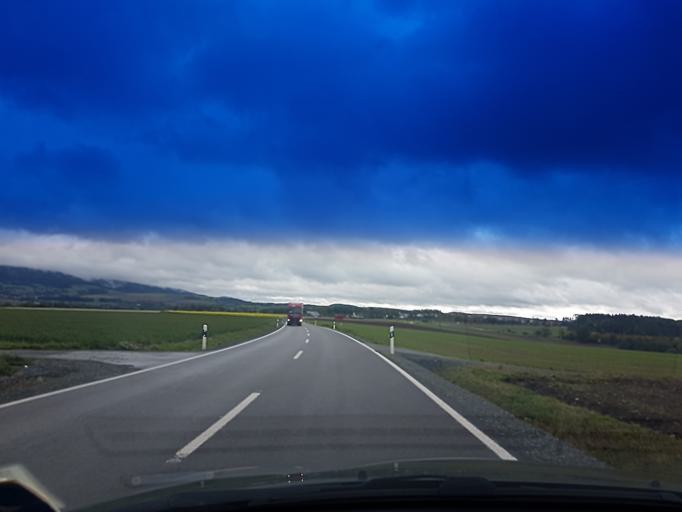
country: DE
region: Bavaria
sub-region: Upper Franconia
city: Bindlach
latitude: 50.0073
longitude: 11.6184
